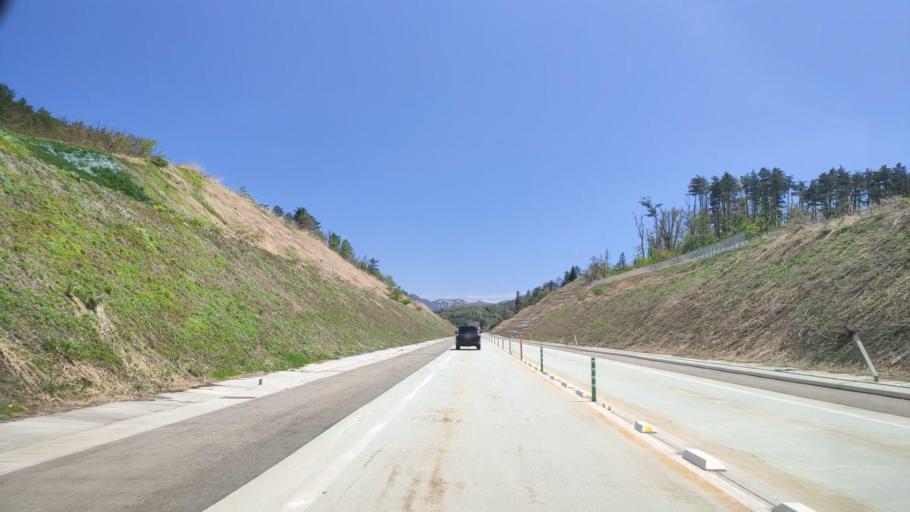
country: JP
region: Yamagata
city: Obanazawa
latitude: 38.5866
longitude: 140.3922
